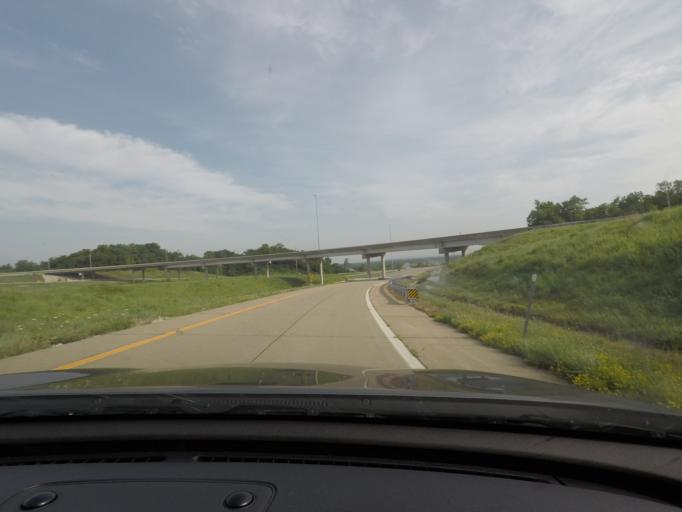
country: US
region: Missouri
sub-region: Saint Charles County
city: Saint Peters
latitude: 38.7999
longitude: -90.5892
